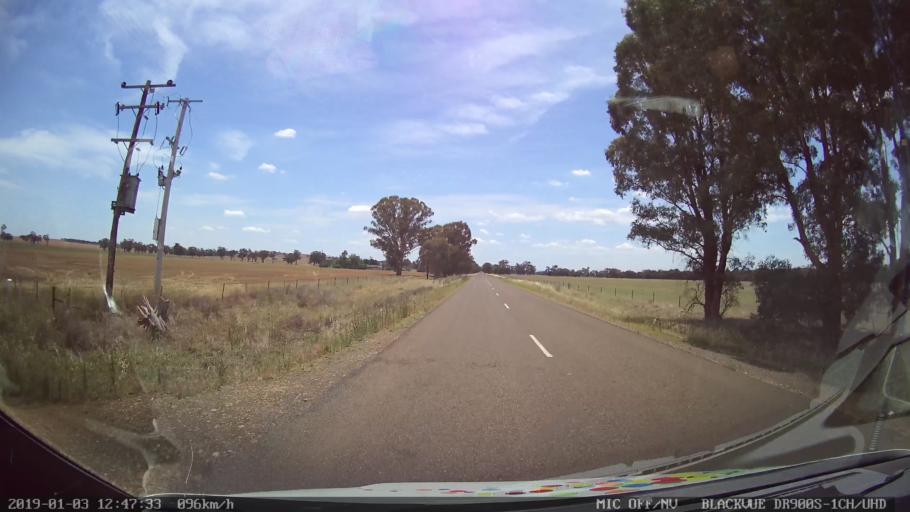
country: AU
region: New South Wales
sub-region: Weddin
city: Grenfell
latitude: -33.7254
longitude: 148.2429
